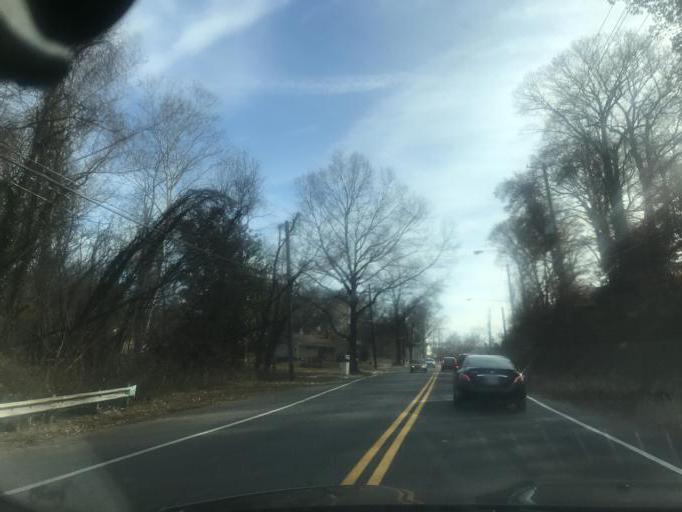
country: US
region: Maryland
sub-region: Prince George's County
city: Forest Heights
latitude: 38.8104
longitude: -76.9919
